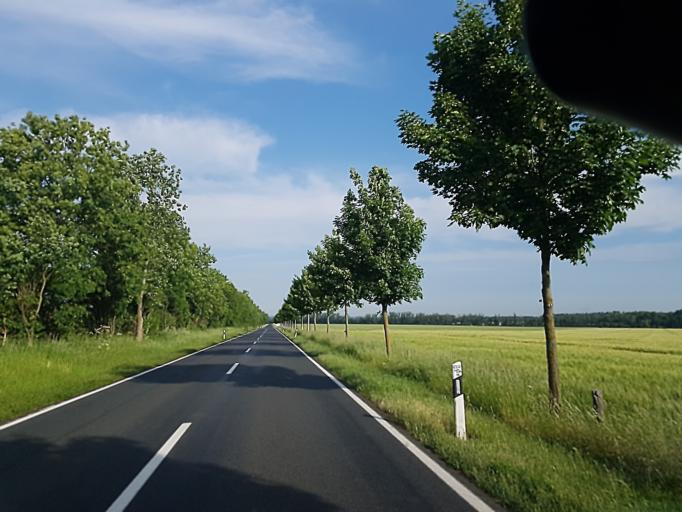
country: DE
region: Brandenburg
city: Niemegk
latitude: 52.0300
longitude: 12.7361
